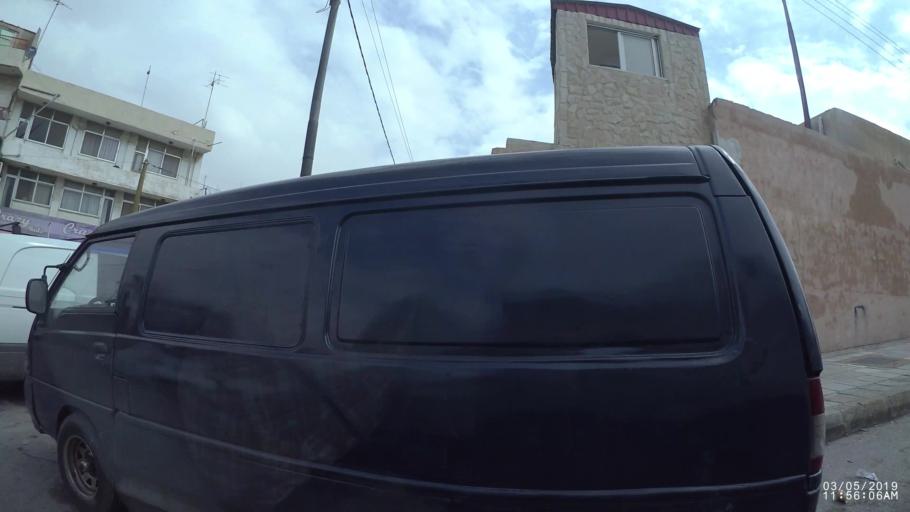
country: JO
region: Amman
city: Amman
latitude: 31.9706
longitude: 35.9293
